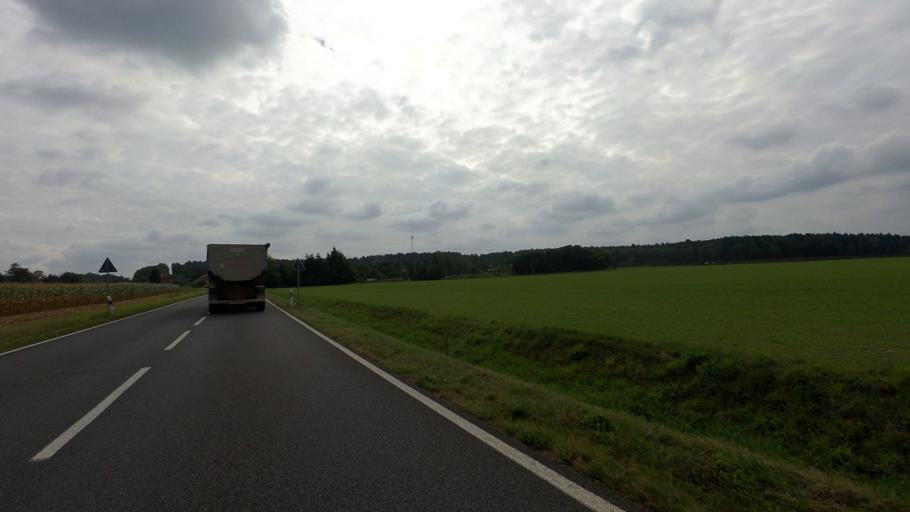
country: DE
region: Brandenburg
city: Kasel-Golzig
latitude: 51.9024
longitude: 13.6753
